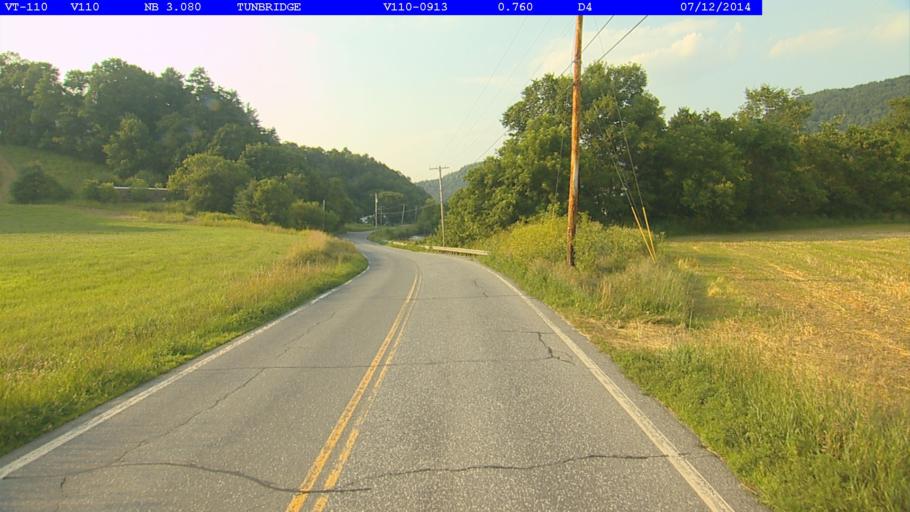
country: US
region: Vermont
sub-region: Orange County
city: Chelsea
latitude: 43.8618
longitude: -72.4996
